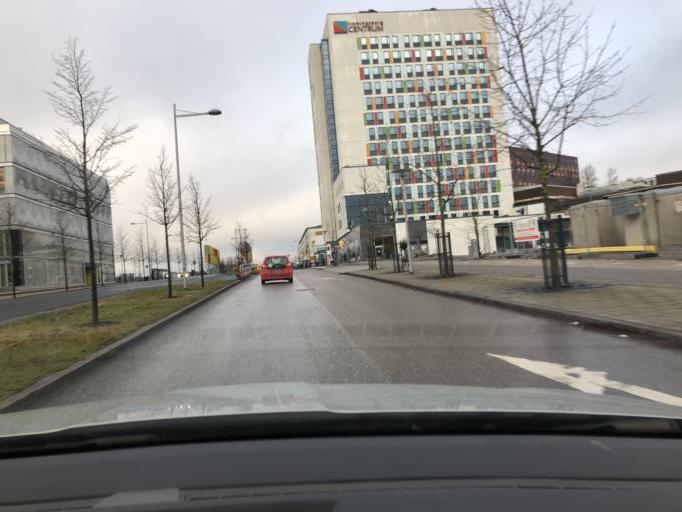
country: SE
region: Stockholm
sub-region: Huddinge Kommun
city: Huddinge
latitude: 59.2218
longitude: 17.9403
